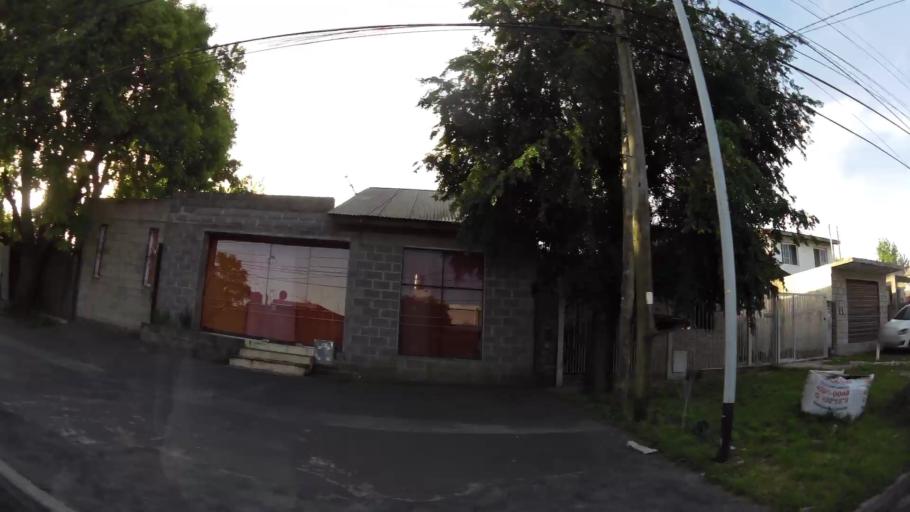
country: AR
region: Buenos Aires
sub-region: Partido de Quilmes
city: Quilmes
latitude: -34.7986
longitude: -58.1979
